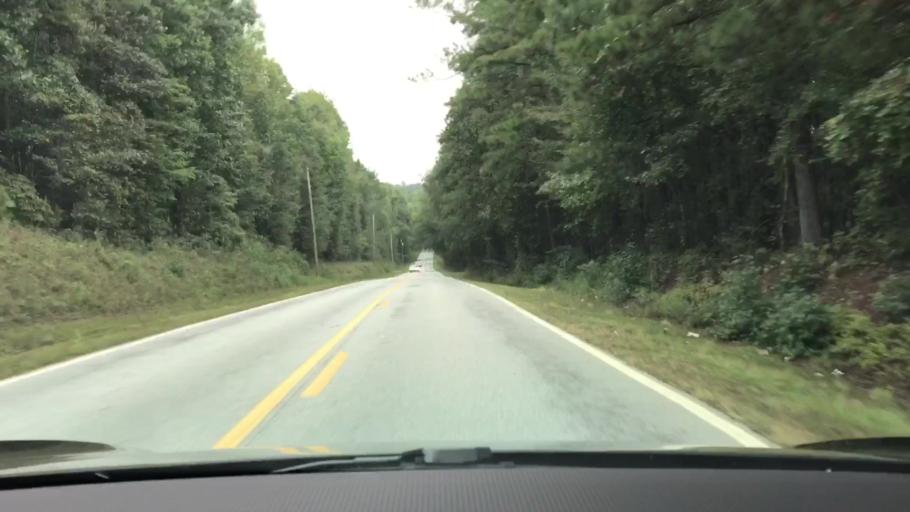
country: US
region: Georgia
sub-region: Barrow County
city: Auburn
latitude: 34.0534
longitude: -83.8215
